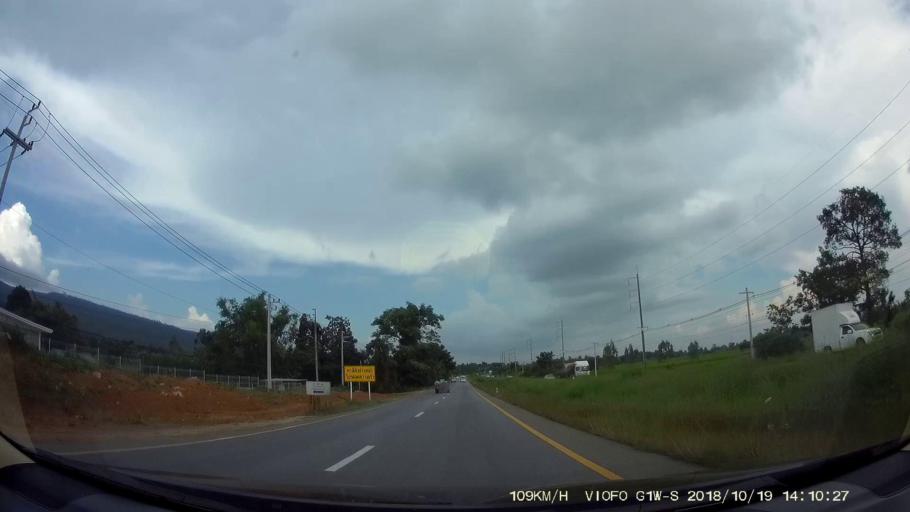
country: TH
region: Chaiyaphum
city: Khon Sawan
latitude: 15.9305
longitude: 102.1464
